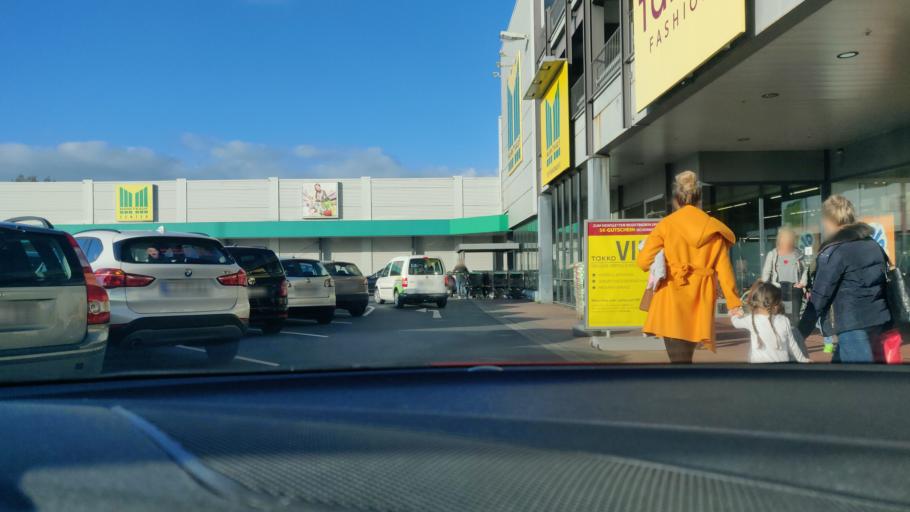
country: DE
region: Lower Saxony
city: Cuxhaven
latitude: 53.8448
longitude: 8.6925
